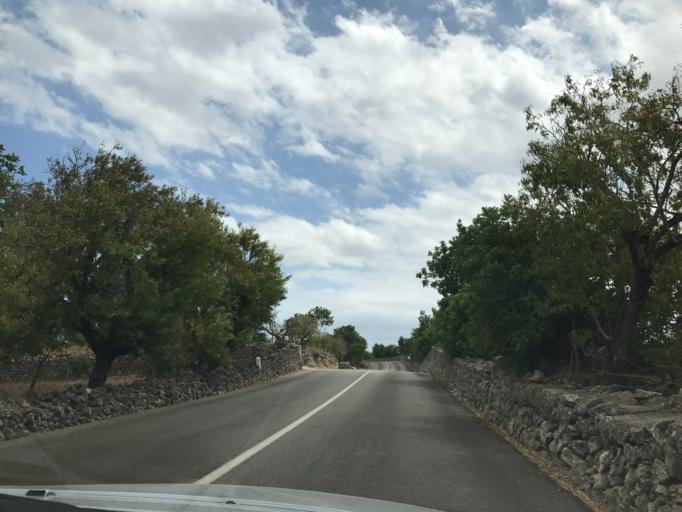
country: ES
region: Balearic Islands
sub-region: Illes Balears
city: Arta
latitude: 39.6660
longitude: 3.3321
